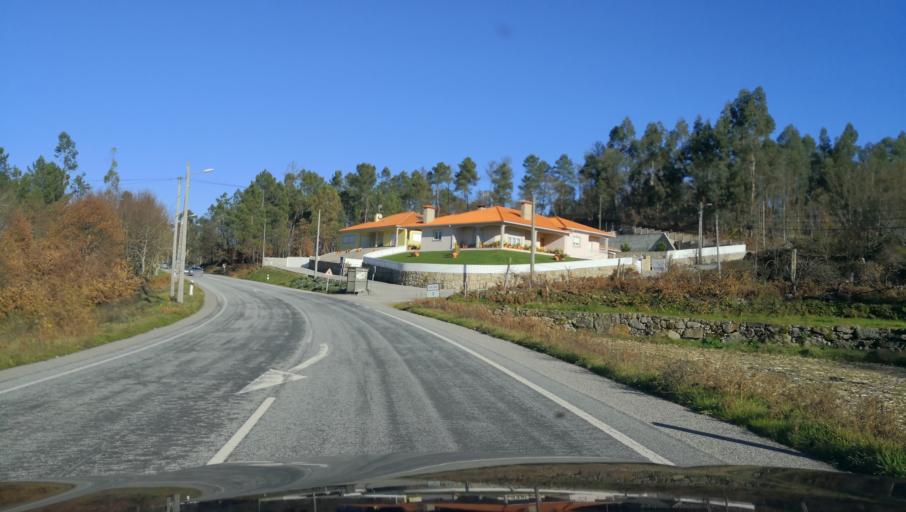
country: PT
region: Viseu
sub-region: Vouzela
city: Vouzela
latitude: 40.7116
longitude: -8.1403
